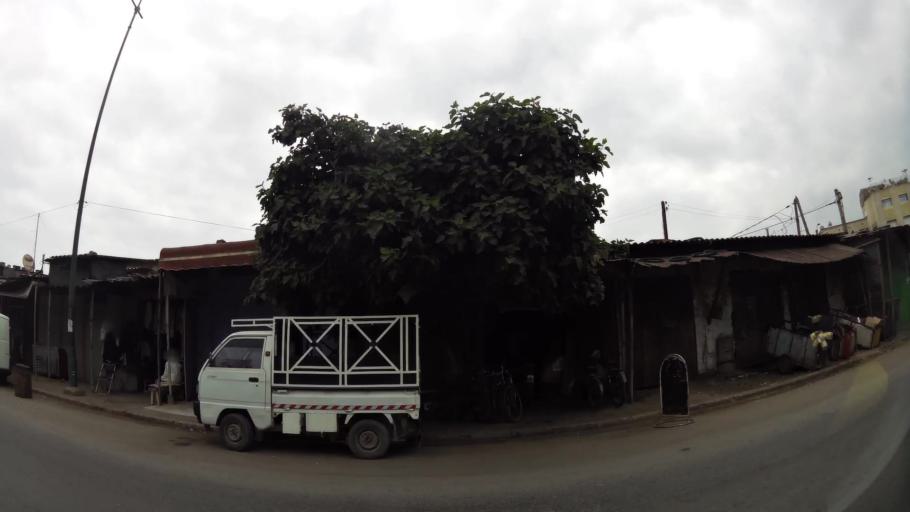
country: MA
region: Rabat-Sale-Zemmour-Zaer
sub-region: Rabat
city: Rabat
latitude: 33.9928
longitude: -6.8716
